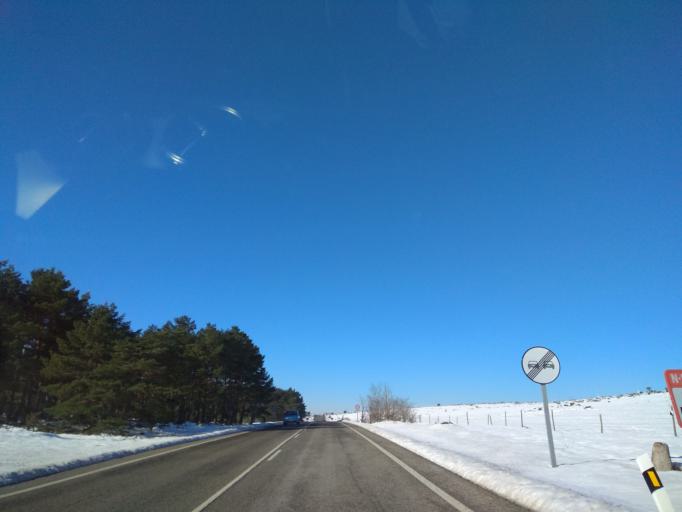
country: ES
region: Castille and Leon
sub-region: Provincia de Burgos
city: Medina de Pomar
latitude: 42.9296
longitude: -3.6488
